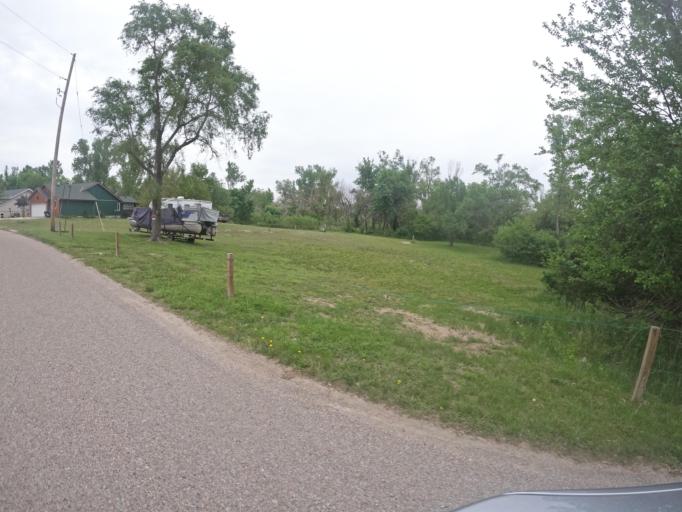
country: US
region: Nebraska
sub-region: Sarpy County
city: Offutt Air Force Base
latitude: 41.0551
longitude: -95.9520
